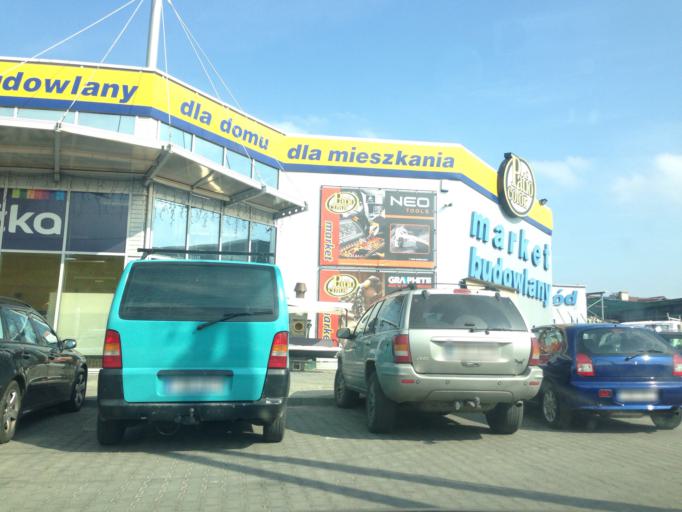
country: PL
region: Kujawsko-Pomorskie
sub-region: Powiat brodnicki
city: Brodnica
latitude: 53.2634
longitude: 19.4018
